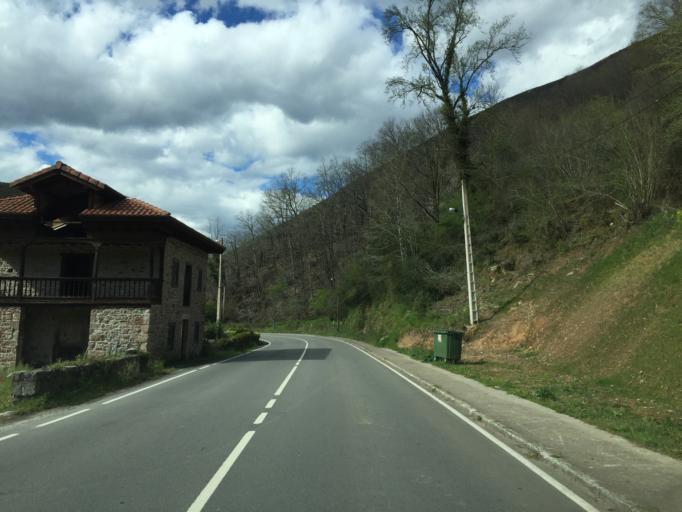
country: ES
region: Asturias
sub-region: Province of Asturias
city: Cangas de Onis
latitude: 43.3270
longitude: -5.0793
